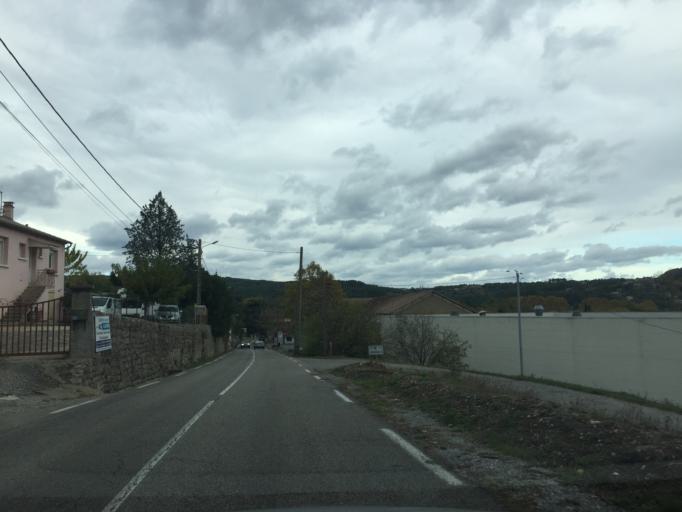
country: FR
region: Rhone-Alpes
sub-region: Departement de l'Ardeche
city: Les Vans
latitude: 44.4100
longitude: 4.1386
